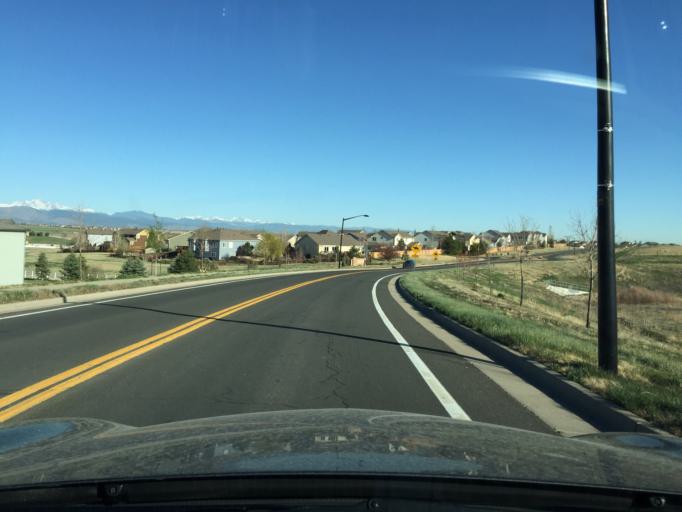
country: US
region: Colorado
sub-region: Boulder County
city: Erie
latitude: 40.0149
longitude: -105.0361
